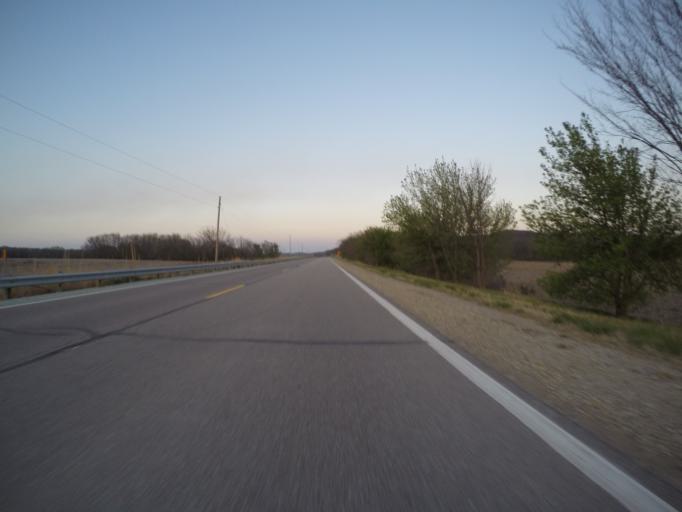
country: US
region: Kansas
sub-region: Riley County
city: Ogden
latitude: 39.1024
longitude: -96.6457
